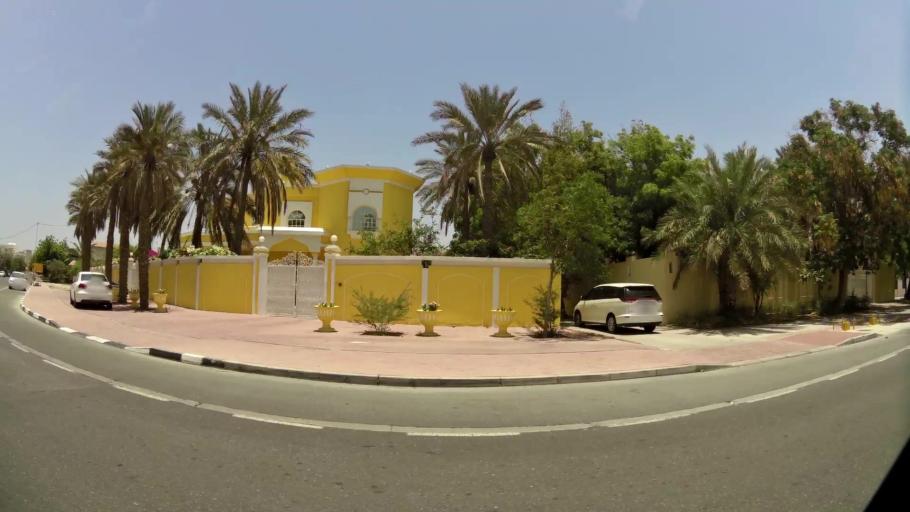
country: AE
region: Ash Shariqah
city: Sharjah
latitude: 25.2386
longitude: 55.2902
